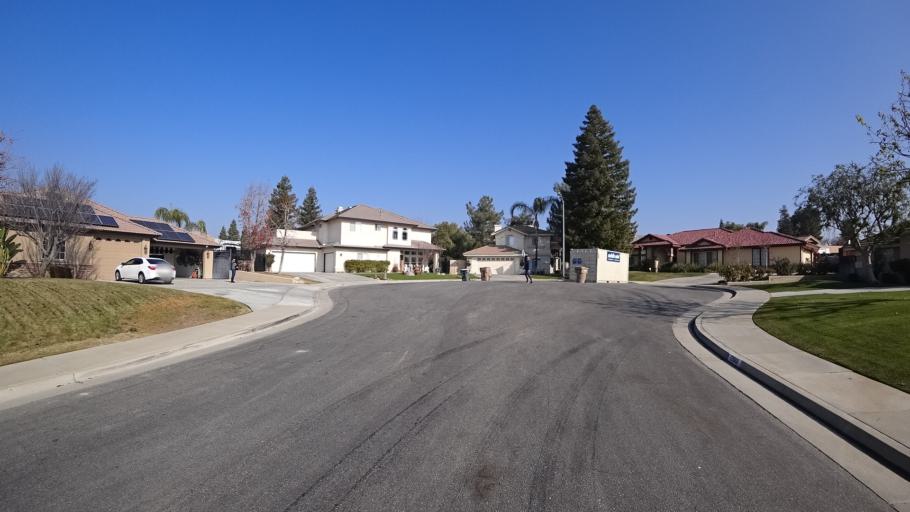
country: US
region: California
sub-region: Kern County
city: Oildale
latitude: 35.4062
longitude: -118.8705
